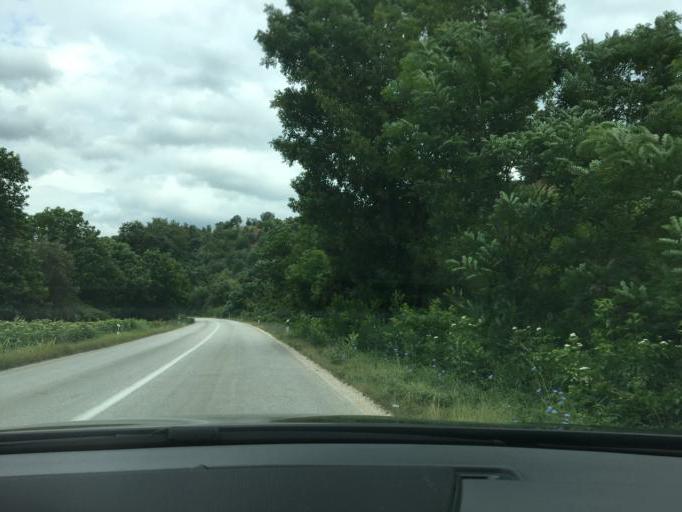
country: MK
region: Kriva Palanka
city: Kriva Palanka
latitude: 42.1767
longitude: 22.2412
